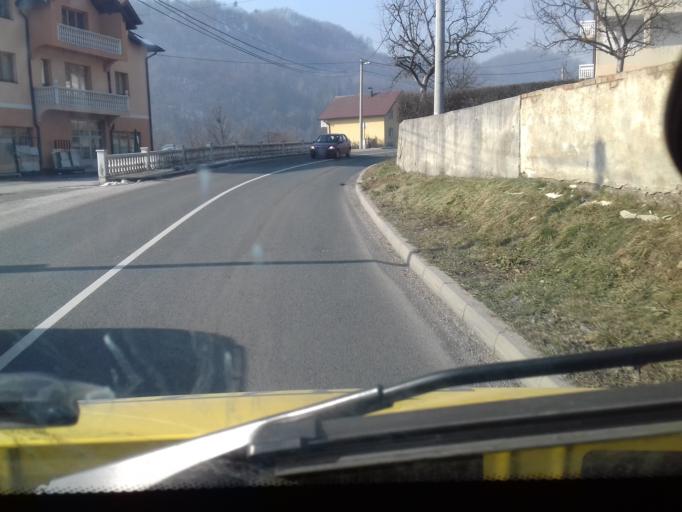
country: BA
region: Federation of Bosnia and Herzegovina
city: Ilijas
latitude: 43.9262
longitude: 18.3067
